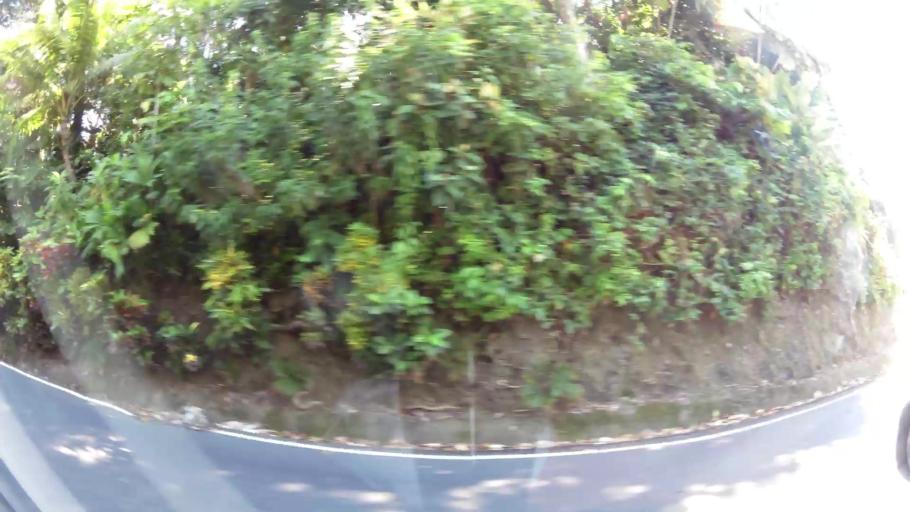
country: CR
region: Puntarenas
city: Quepos
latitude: 9.3985
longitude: -84.1550
